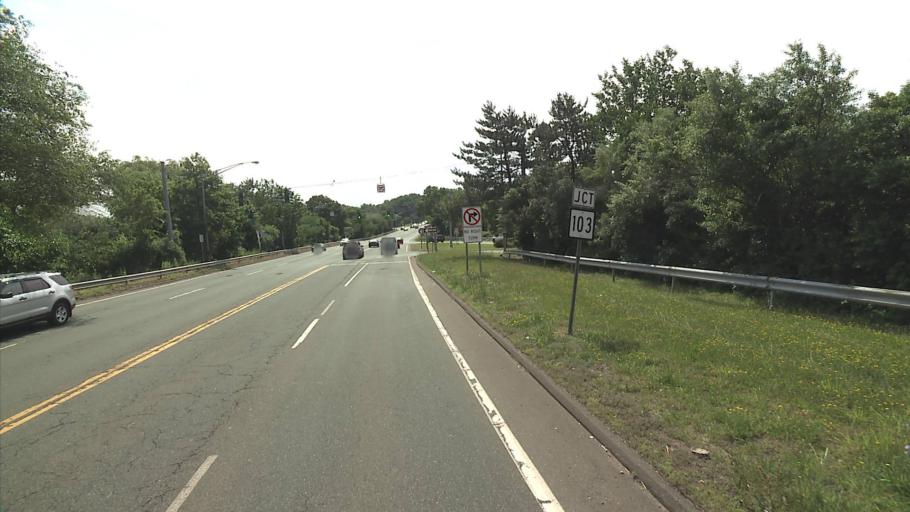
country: US
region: Connecticut
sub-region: New Haven County
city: North Haven
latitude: 41.3919
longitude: -72.8627
